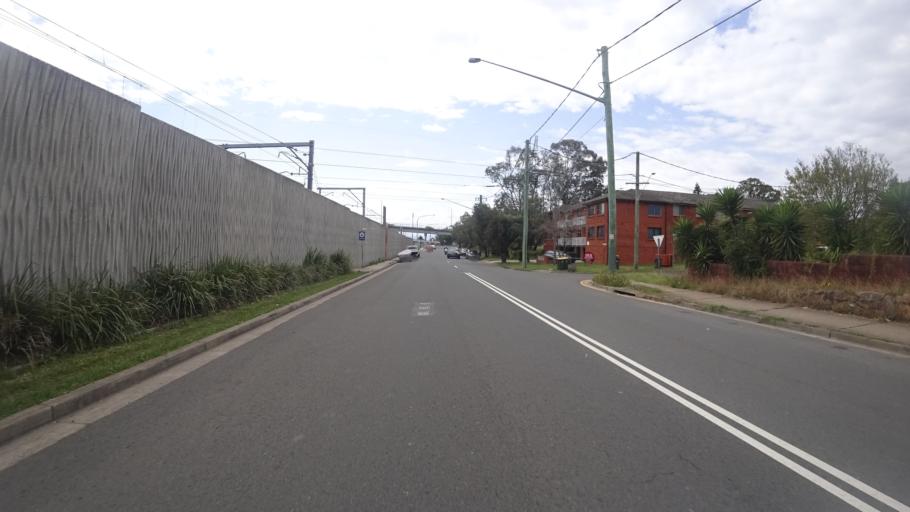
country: AU
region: New South Wales
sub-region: Campbelltown Municipality
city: Glenfield
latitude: -33.9679
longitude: 150.8983
